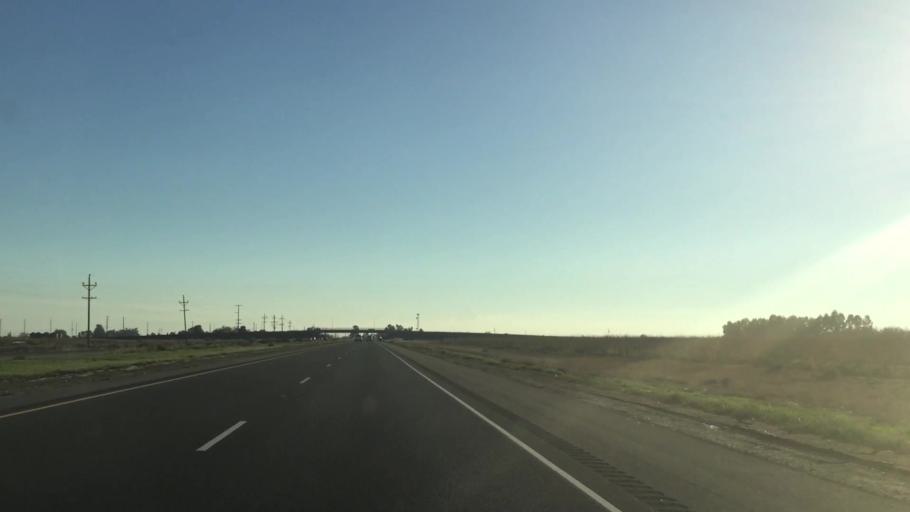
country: US
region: California
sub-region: Yuba County
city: Plumas Lake
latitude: 38.9325
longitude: -121.5440
